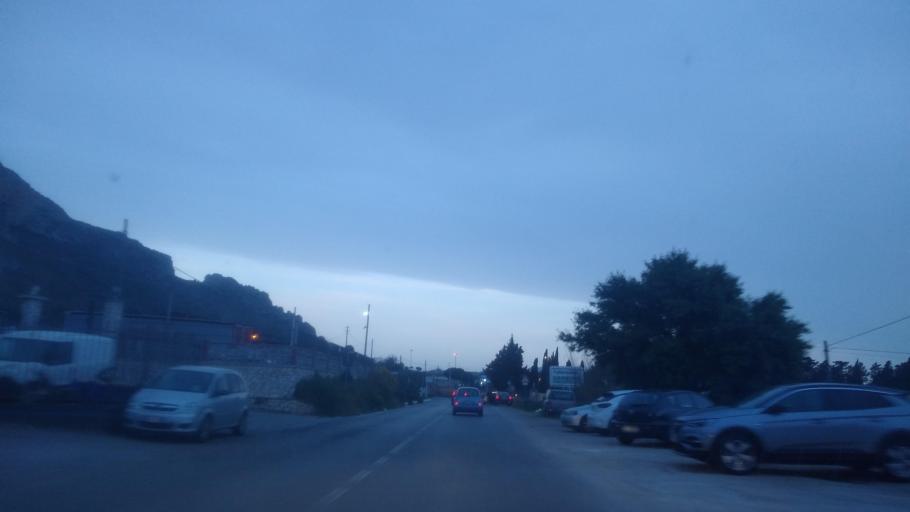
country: IT
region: Sicily
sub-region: Palermo
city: Terrasini
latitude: 38.1433
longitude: 13.0861
